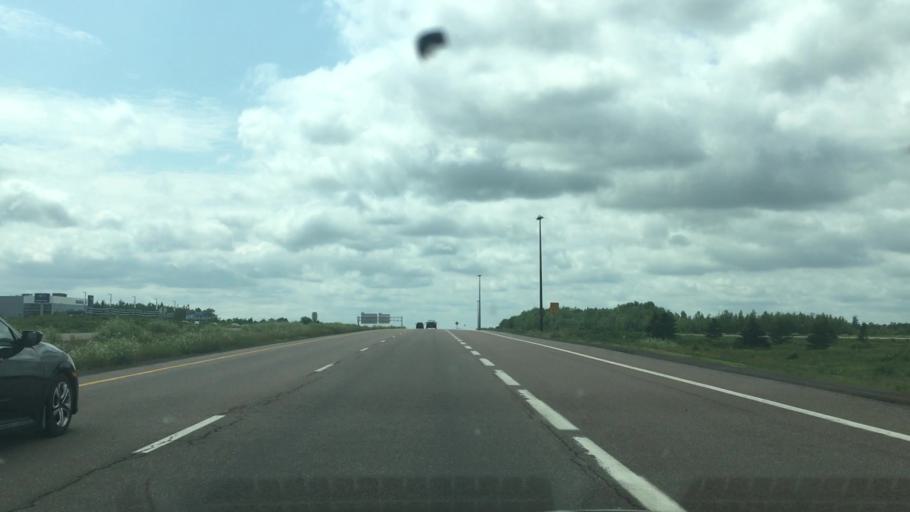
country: CA
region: New Brunswick
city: Dieppe
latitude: 46.1267
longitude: -64.6828
